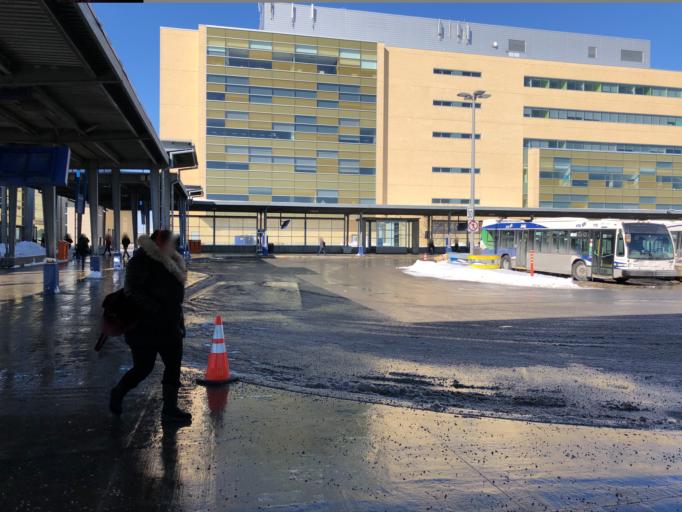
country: CA
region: Quebec
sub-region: Laval
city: Laval
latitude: 45.5579
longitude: -73.7207
